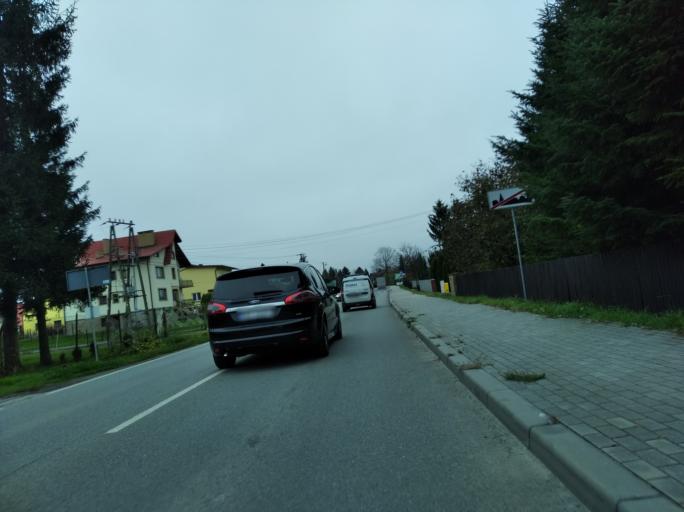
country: PL
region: Subcarpathian Voivodeship
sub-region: Powiat krosnienski
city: Chorkowka
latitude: 49.6777
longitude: 21.7107
